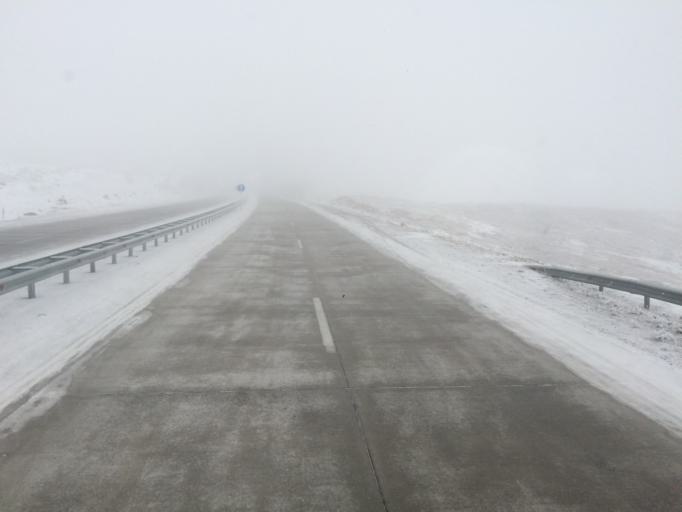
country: KZ
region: Zhambyl
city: Georgiyevka
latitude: 43.4211
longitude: 74.9695
